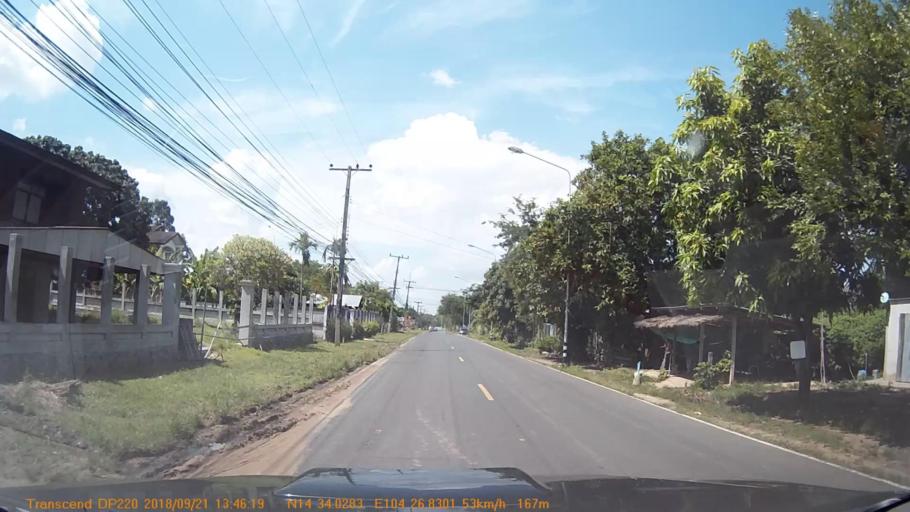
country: TH
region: Sisaket
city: Khun Han
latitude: 14.5674
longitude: 104.4471
